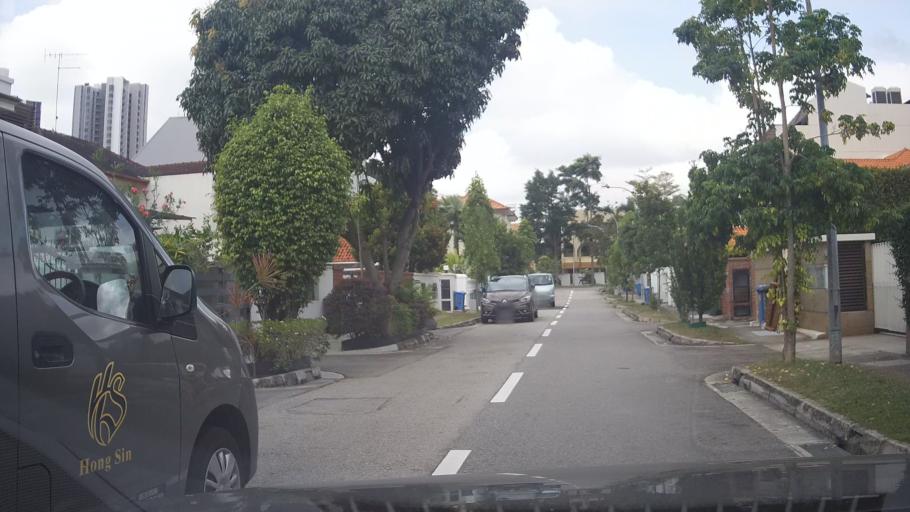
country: SG
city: Singapore
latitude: 1.2999
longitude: 103.8952
